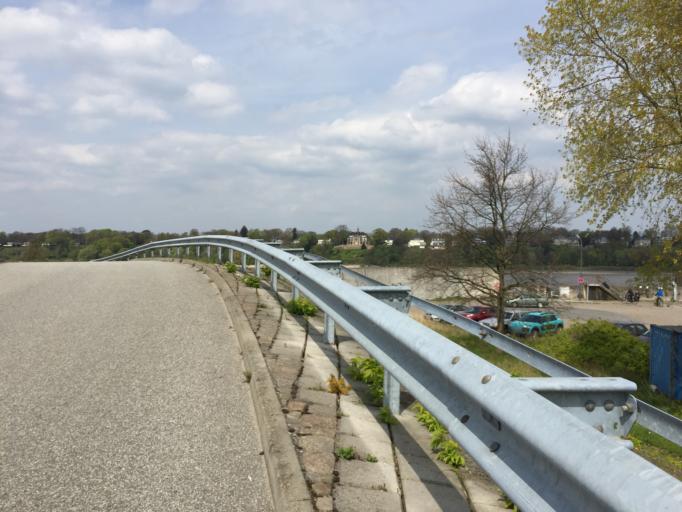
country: DE
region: Hamburg
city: Altona
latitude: 53.5391
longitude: 9.8844
